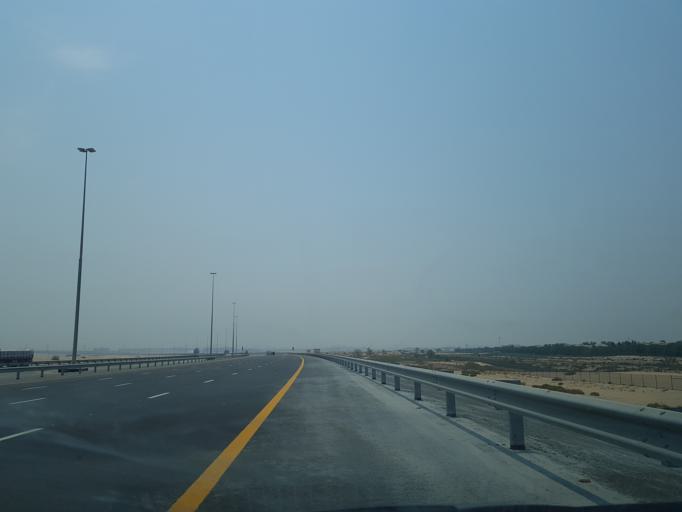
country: AE
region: Dubai
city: Dubai
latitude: 25.0108
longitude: 55.2063
